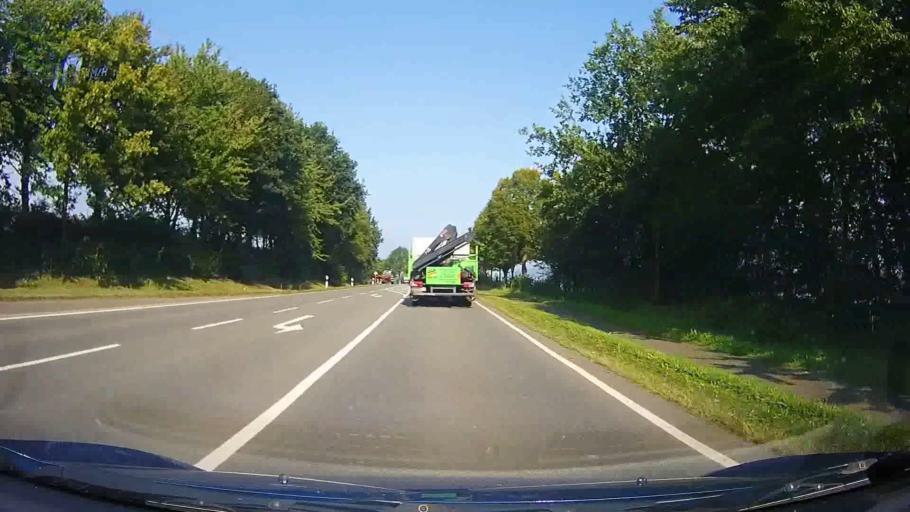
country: DE
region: Lower Saxony
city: Moringen
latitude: 51.6844
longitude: 9.8616
